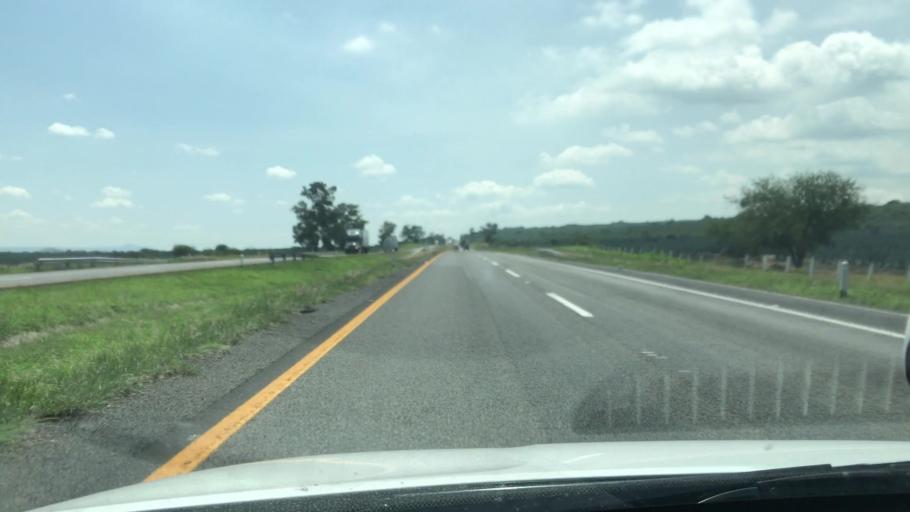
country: MX
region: Jalisco
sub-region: Poncitlan
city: Santa Cruz el Grande
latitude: 20.4425
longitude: -102.8564
